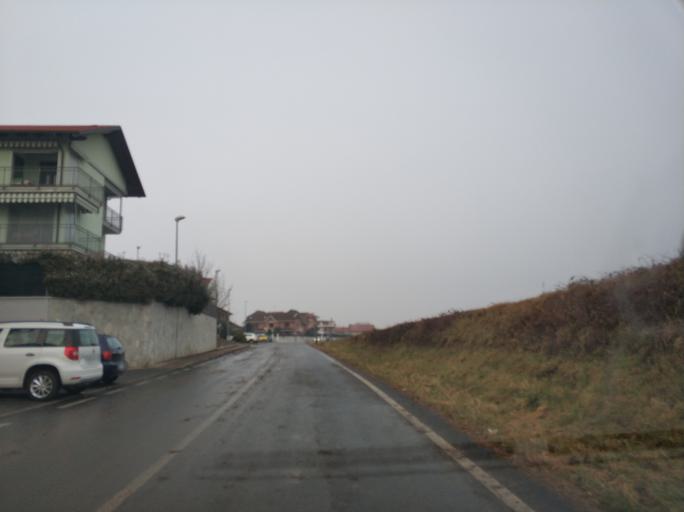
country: IT
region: Piedmont
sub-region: Provincia di Torino
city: San Francesco al Campo
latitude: 45.2243
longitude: 7.6616
